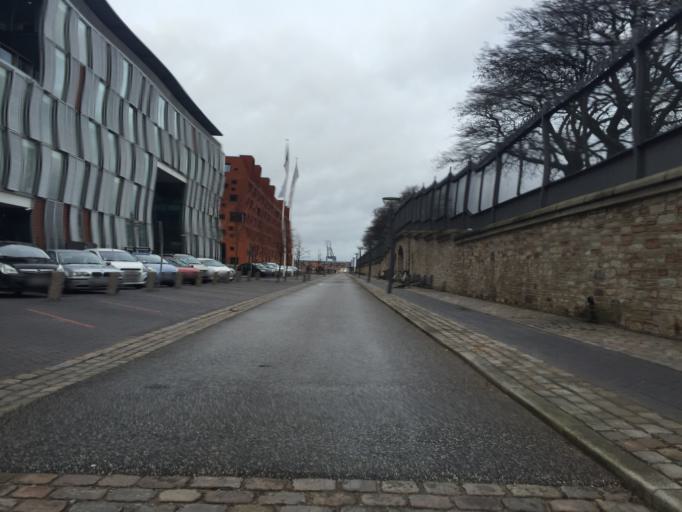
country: DK
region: Capital Region
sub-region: Kobenhavn
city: Christianshavn
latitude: 55.7003
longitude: 12.6003
